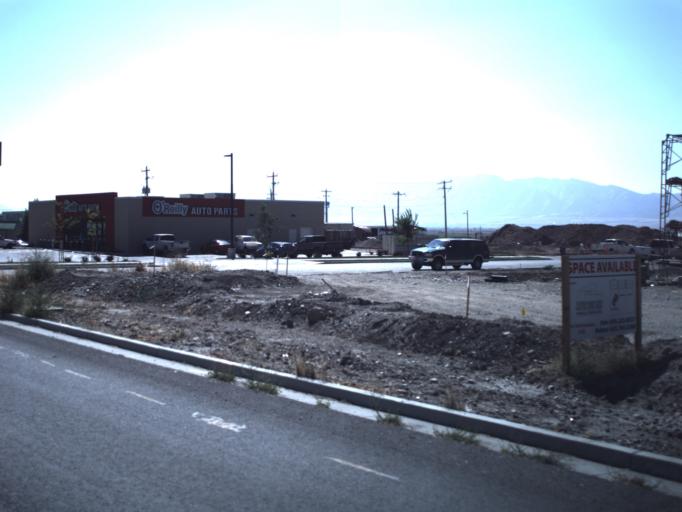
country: US
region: Utah
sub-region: Cache County
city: Smithfield
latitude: 41.8207
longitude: -111.8331
